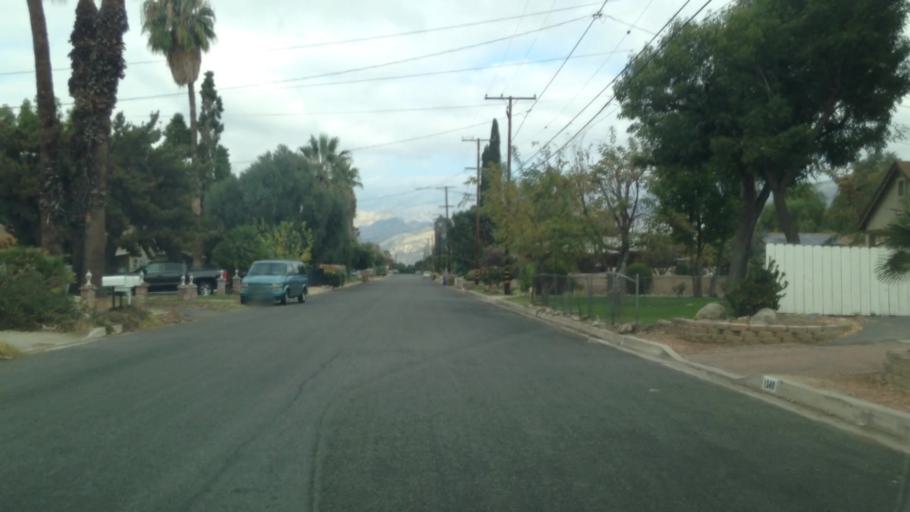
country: US
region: California
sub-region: San Bernardino County
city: Mentone
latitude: 34.0728
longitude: -117.1375
